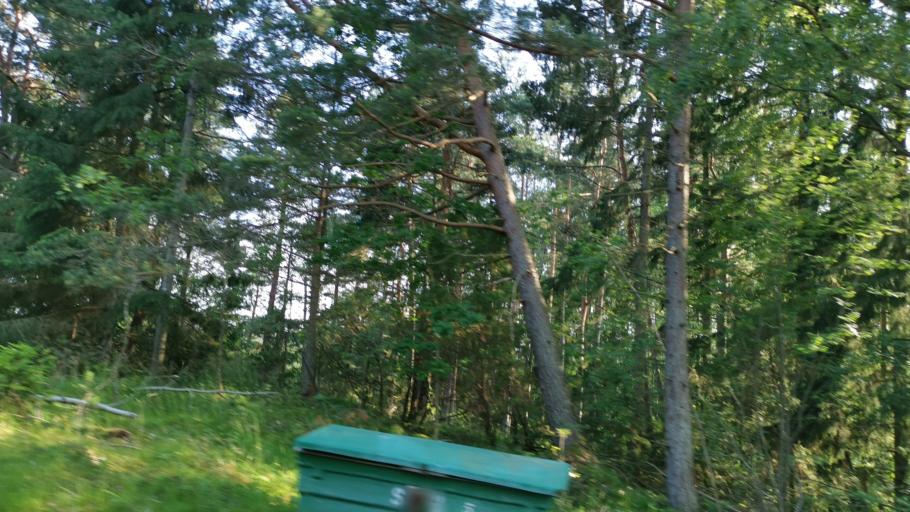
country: SE
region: Vaestra Goetaland
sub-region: Orust
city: Henan
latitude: 58.2862
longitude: 11.6560
